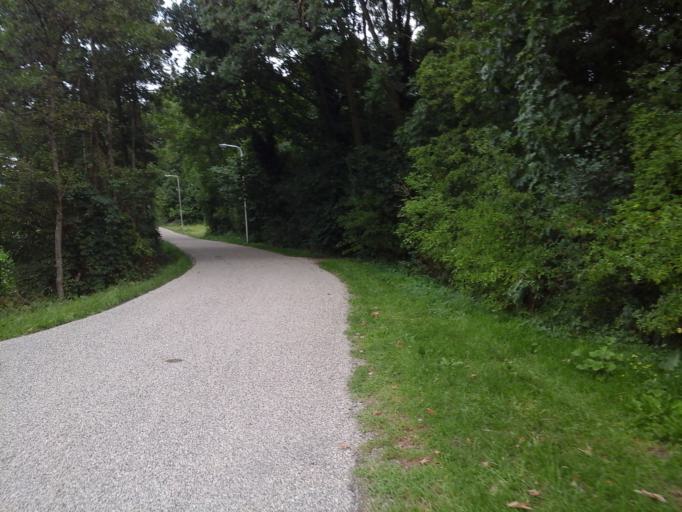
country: NL
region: Gelderland
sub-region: Gemeente Geldermalsen
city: Geldermalsen
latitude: 51.8859
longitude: 5.2777
